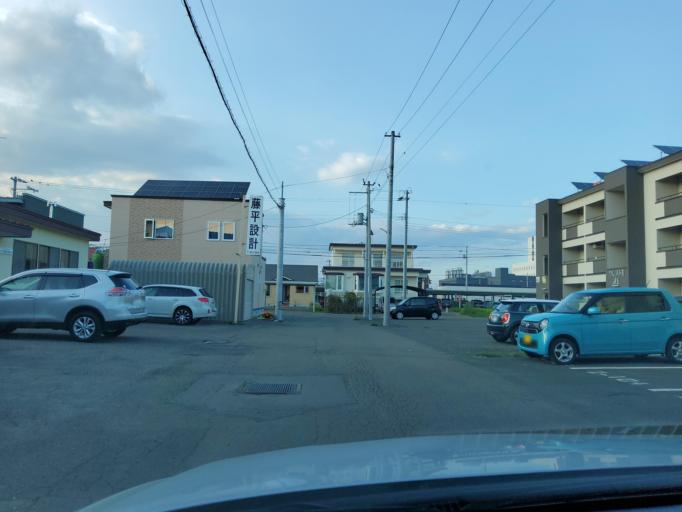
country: JP
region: Hokkaido
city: Obihiro
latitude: 42.9168
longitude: 143.1796
